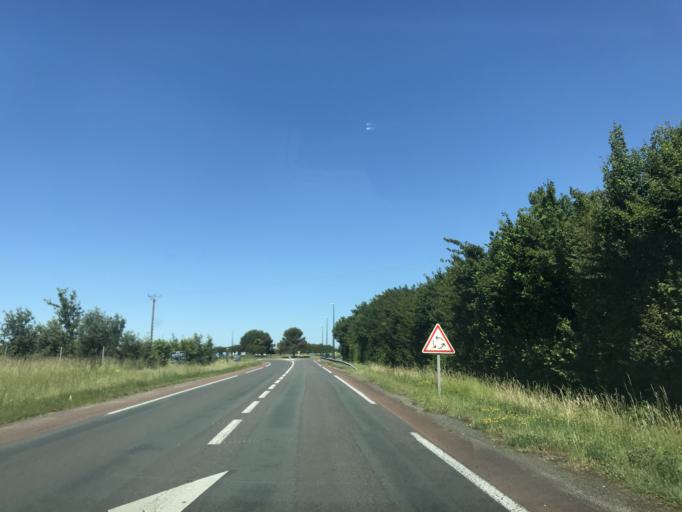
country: FR
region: Poitou-Charentes
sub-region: Departement de la Charente-Maritime
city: Gemozac
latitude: 45.5764
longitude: -0.6734
